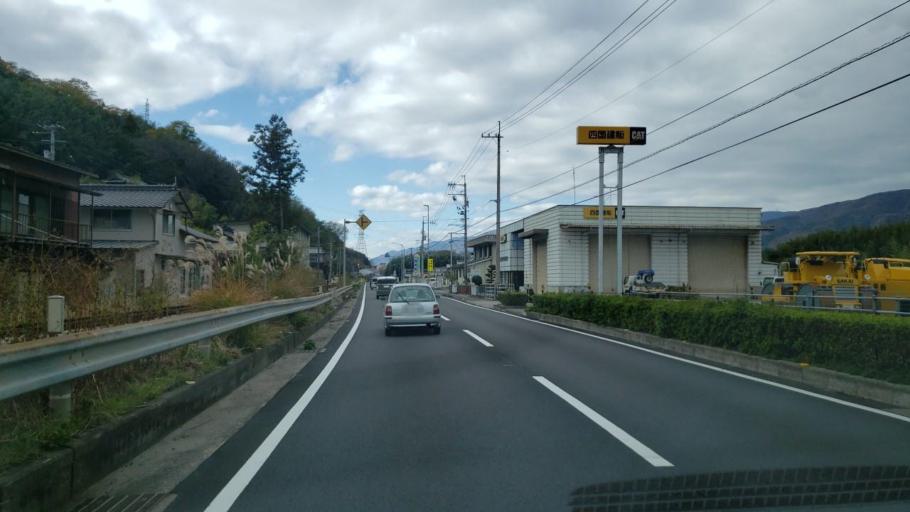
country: JP
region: Tokushima
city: Wakimachi
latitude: 34.0548
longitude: 134.1393
